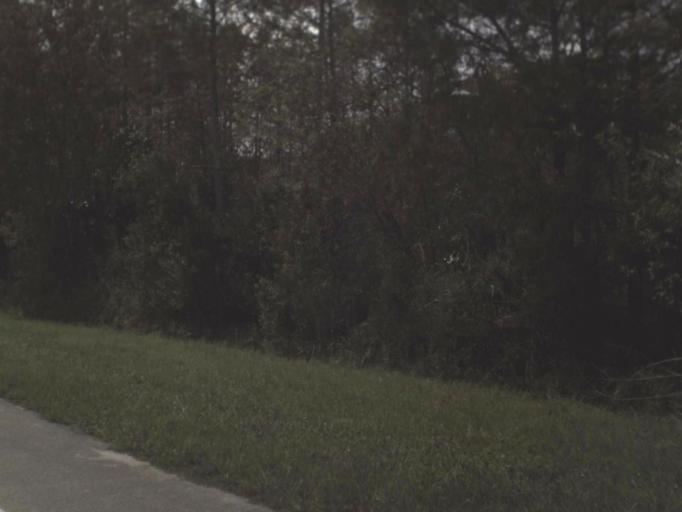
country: US
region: Florida
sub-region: Collier County
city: Orangetree
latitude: 26.0617
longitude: -81.3446
